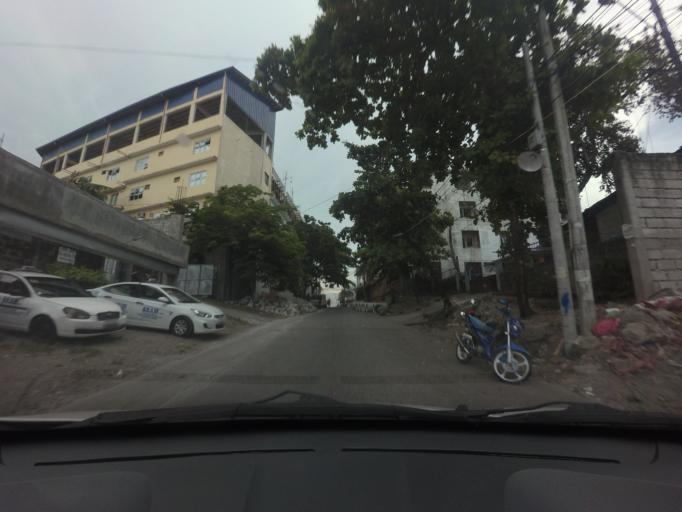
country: PH
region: Calabarzon
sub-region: Province of Rizal
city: Taguig
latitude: 14.5033
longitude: 121.0545
